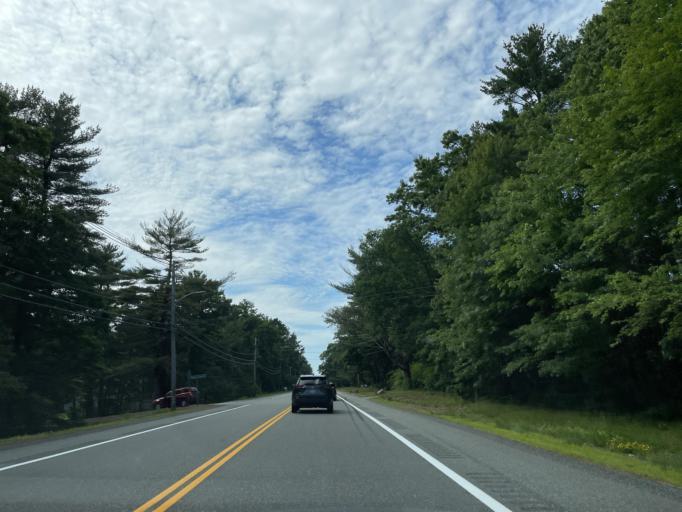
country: US
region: Rhode Island
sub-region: Kent County
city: West Greenwich
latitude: 41.6348
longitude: -71.6858
